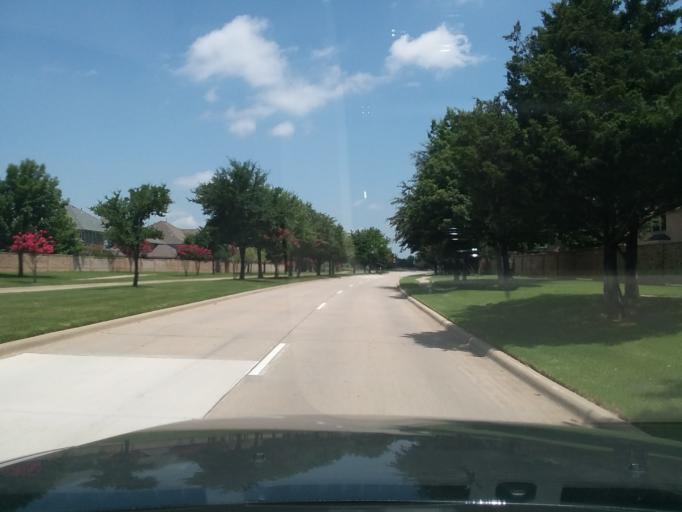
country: US
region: Texas
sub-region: Denton County
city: Bartonville
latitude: 33.0936
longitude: -97.1234
